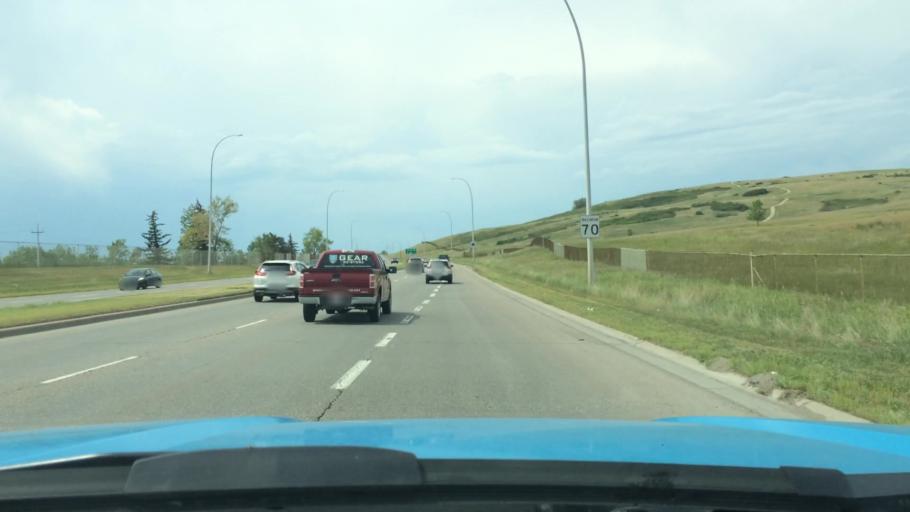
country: CA
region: Alberta
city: Calgary
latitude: 51.0912
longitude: -114.1002
